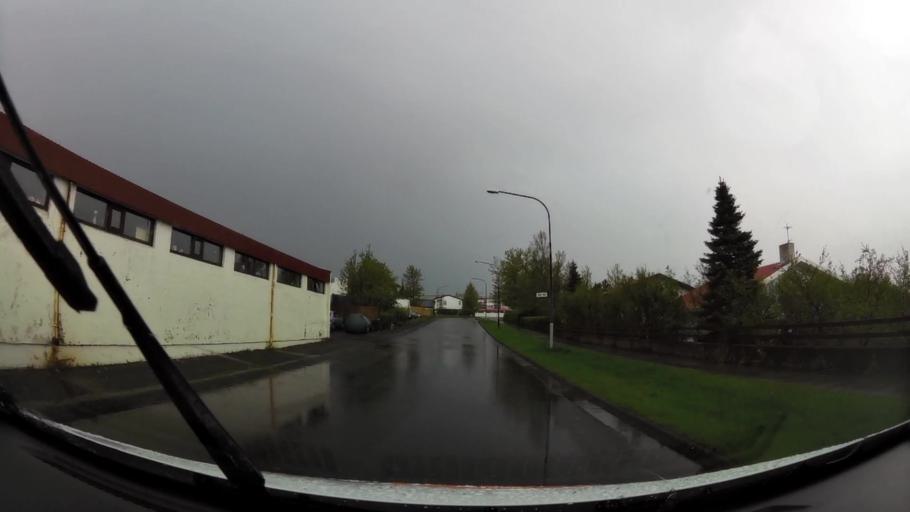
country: IS
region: Capital Region
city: Reykjavik
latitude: 64.1061
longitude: -21.8072
